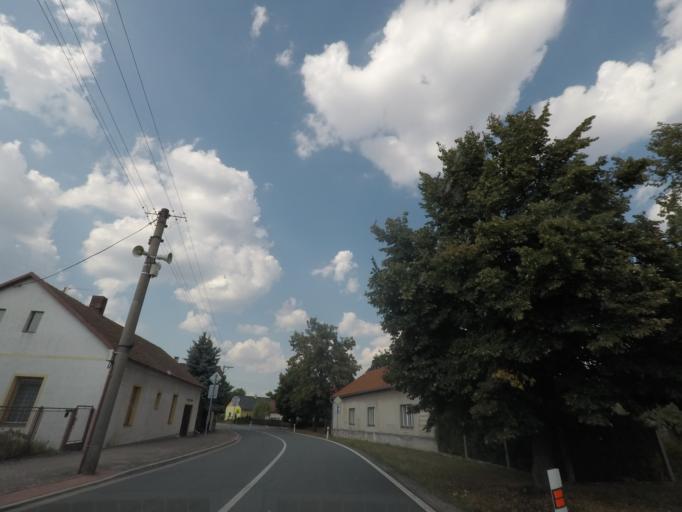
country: CZ
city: Albrechtice nad Orlici
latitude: 50.1201
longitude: 16.0693
